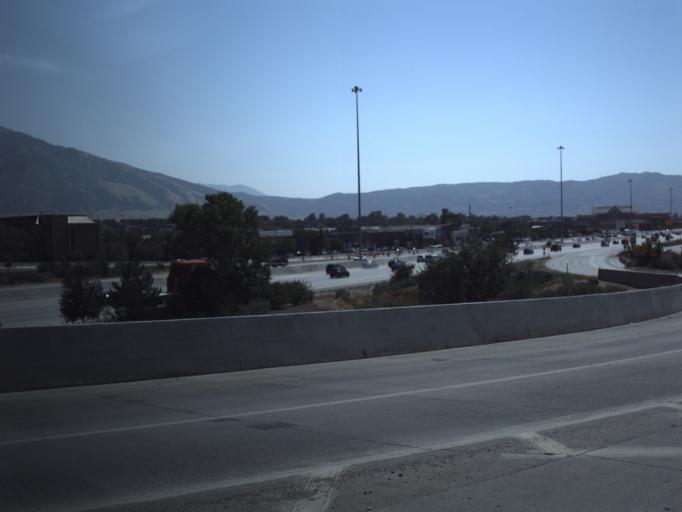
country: US
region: Utah
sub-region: Salt Lake County
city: South Jordan
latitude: 40.5584
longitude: -111.8992
